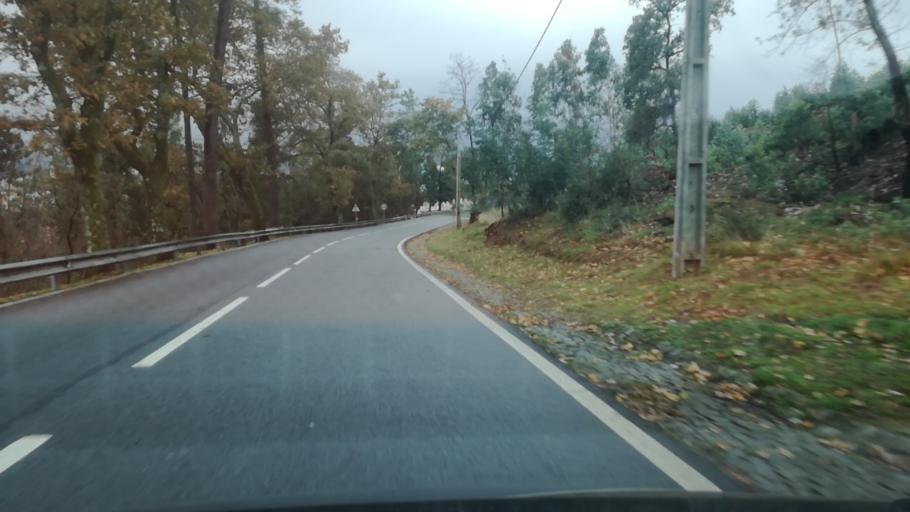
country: PT
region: Braga
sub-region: Braga
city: Braga
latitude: 41.5293
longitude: -8.3931
